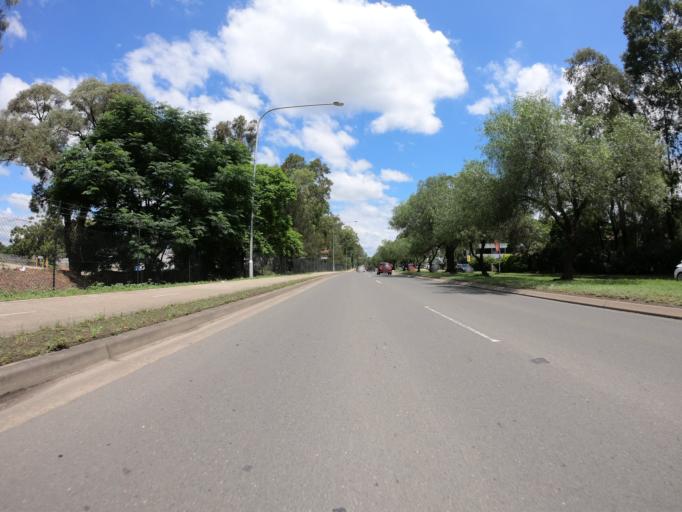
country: AU
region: New South Wales
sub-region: Penrith Municipality
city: Penrith
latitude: -33.7556
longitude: 150.6869
